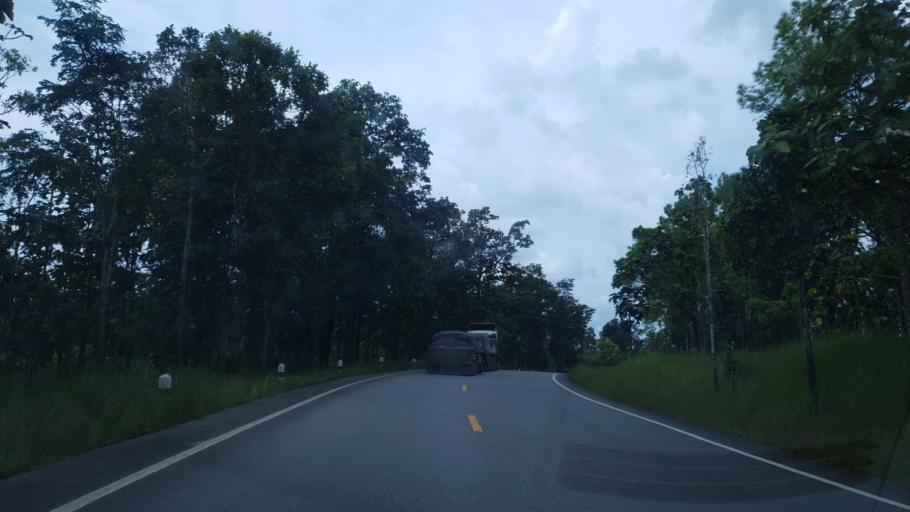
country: TH
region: Mae Hong Son
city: Khun Yuam
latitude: 18.7914
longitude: 97.9338
